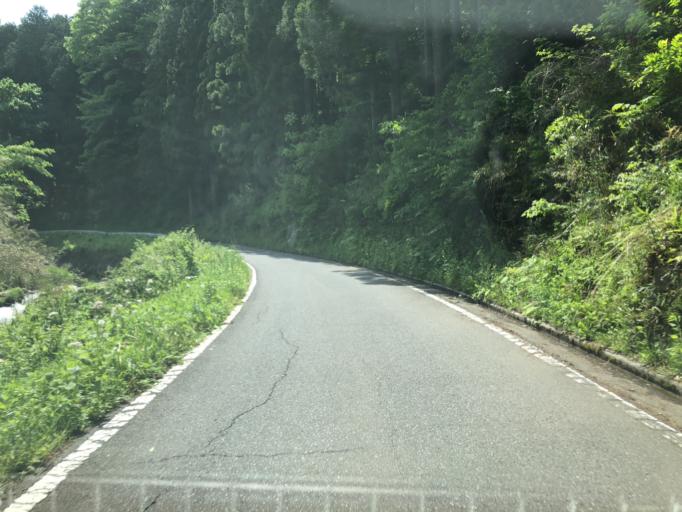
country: JP
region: Fukushima
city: Ishikawa
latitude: 37.0335
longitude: 140.5653
